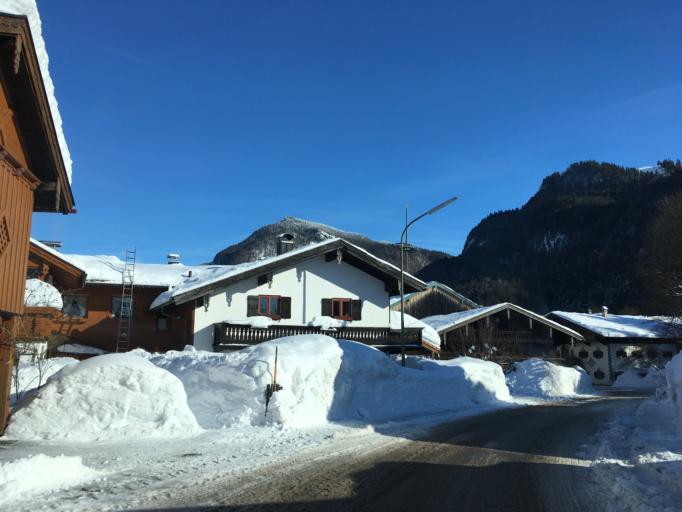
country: AT
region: Tyrol
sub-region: Politischer Bezirk Kufstein
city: Rettenschoss
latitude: 47.6905
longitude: 12.2619
